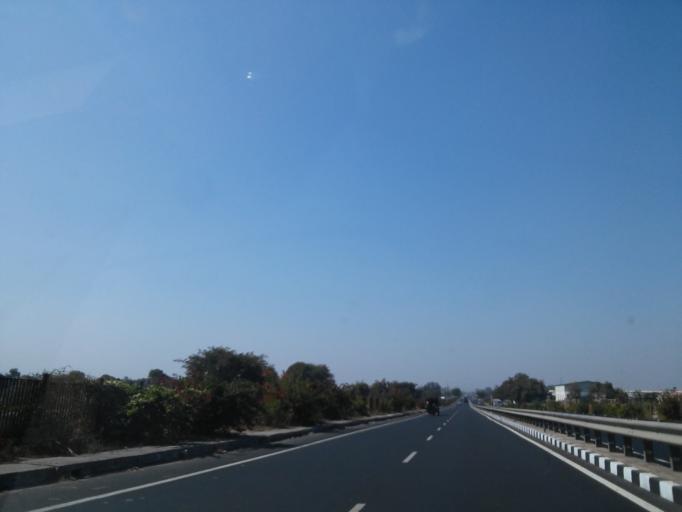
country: IN
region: Gujarat
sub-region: Sabar Kantha
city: Himatnagar
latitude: 23.5812
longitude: 72.9986
